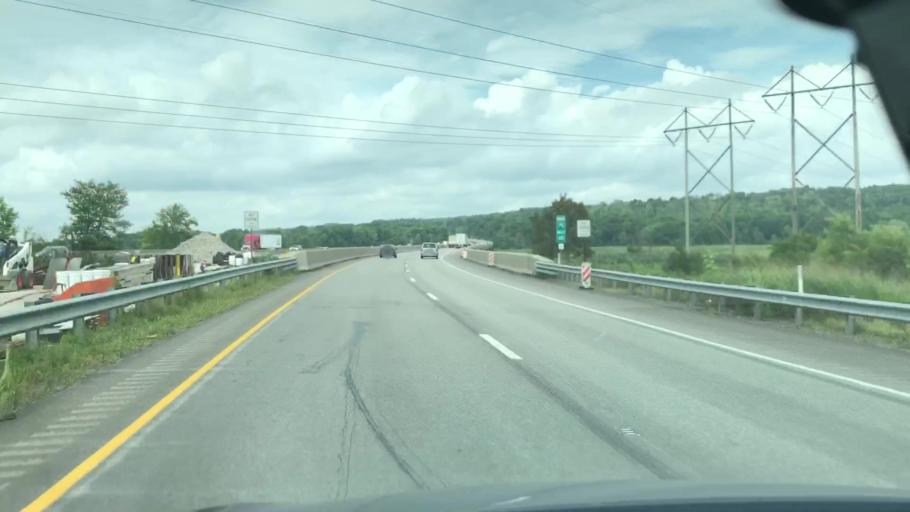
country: US
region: Pennsylvania
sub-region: Crawford County
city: Meadville
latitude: 41.5417
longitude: -80.1833
